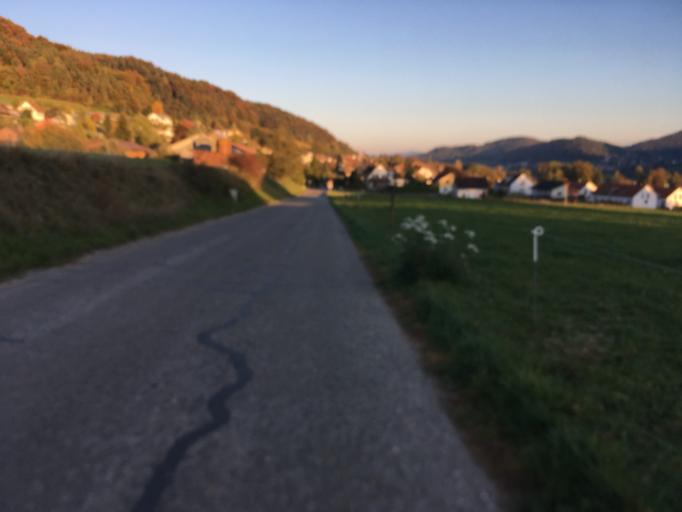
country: CH
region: Zurich
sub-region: Bezirk Buelach
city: Embrach / Kellersacker
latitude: 47.5265
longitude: 8.6162
